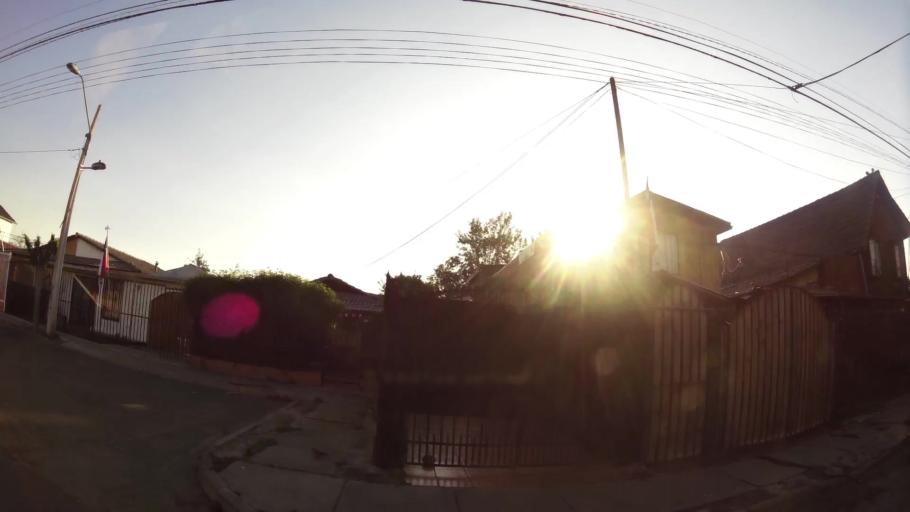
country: CL
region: Santiago Metropolitan
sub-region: Provincia de Santiago
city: La Pintana
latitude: -33.5540
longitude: -70.6186
